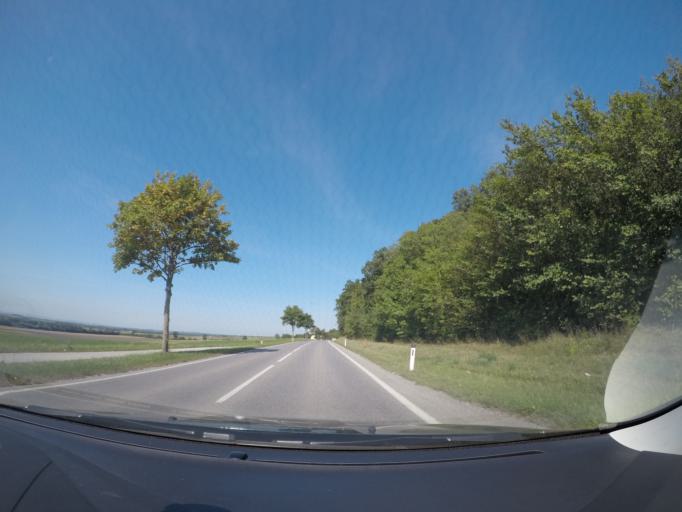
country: AT
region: Lower Austria
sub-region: Politischer Bezirk Bruck an der Leitha
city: Hof am Leithaberge
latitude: 47.9518
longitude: 16.5850
